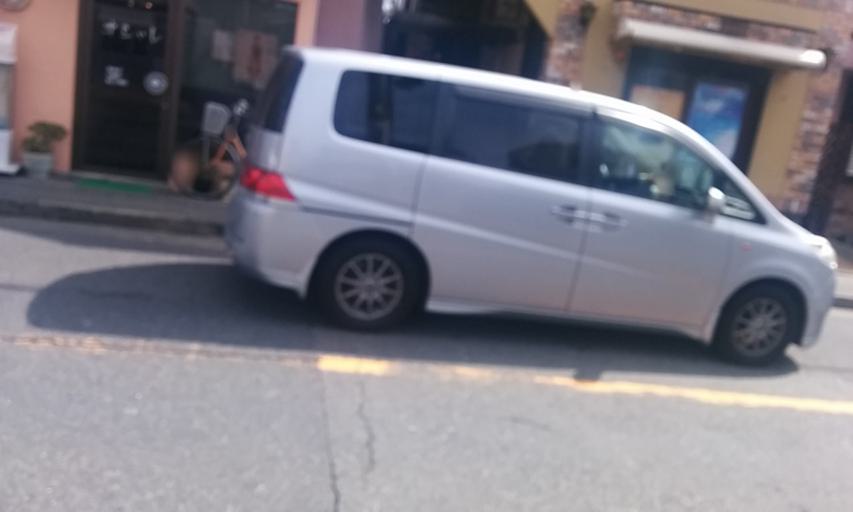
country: JP
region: Kanagawa
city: Kamakura
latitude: 35.3106
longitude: 139.5359
